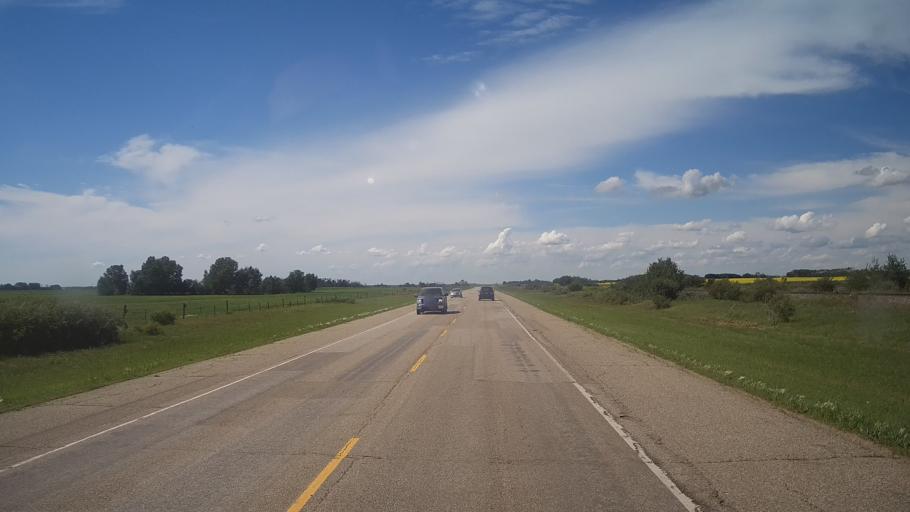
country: CA
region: Saskatchewan
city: Yorkton
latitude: 51.0720
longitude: -102.2285
